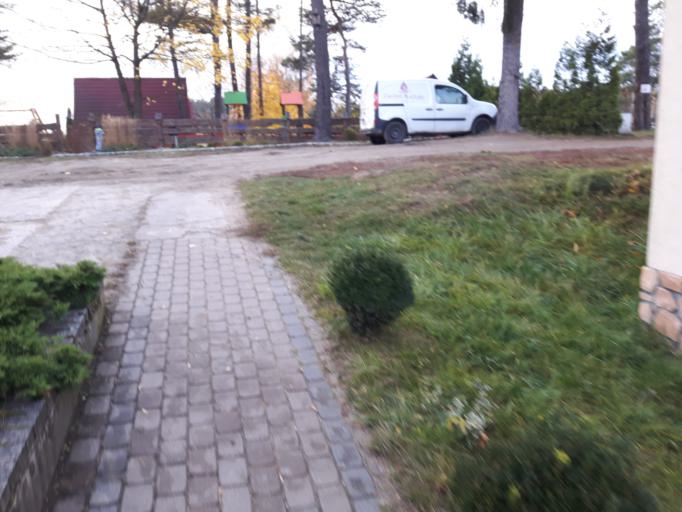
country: PL
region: Warmian-Masurian Voivodeship
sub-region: Powiat olsztynski
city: Barczewo
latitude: 53.8308
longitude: 20.7374
